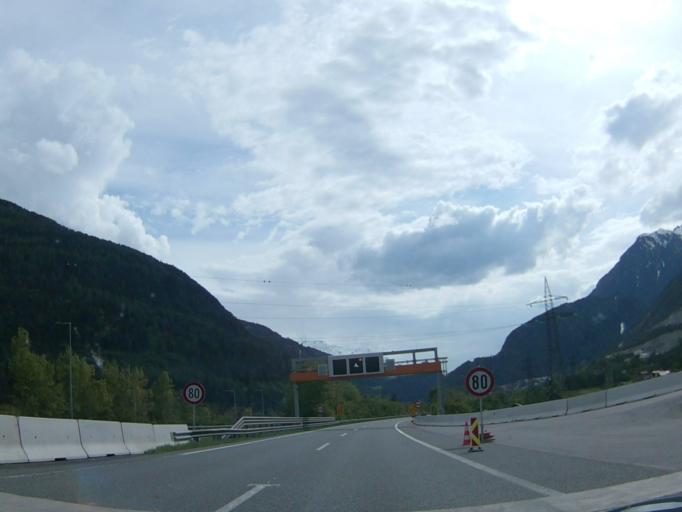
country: AT
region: Tyrol
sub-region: Politischer Bezirk Landeck
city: Schonwies
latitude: 47.2032
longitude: 10.6644
